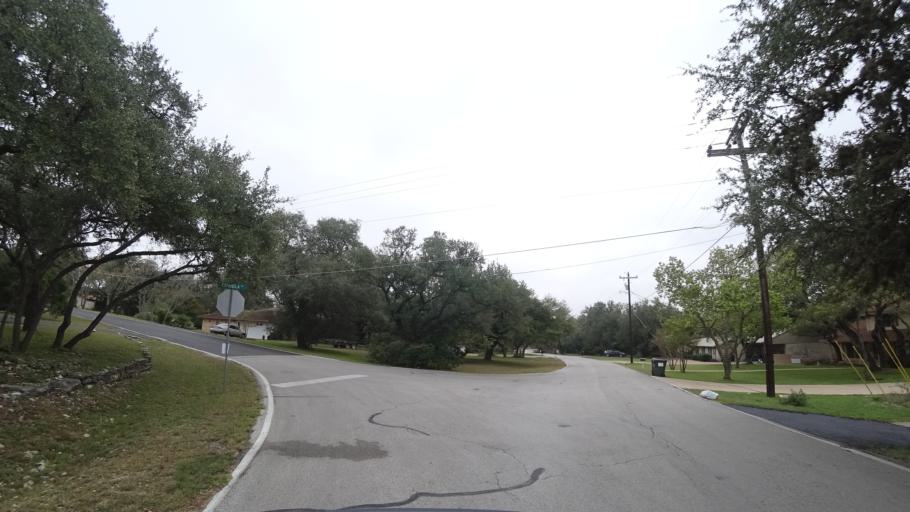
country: US
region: Texas
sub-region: Travis County
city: Barton Creek
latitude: 30.2239
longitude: -97.9023
